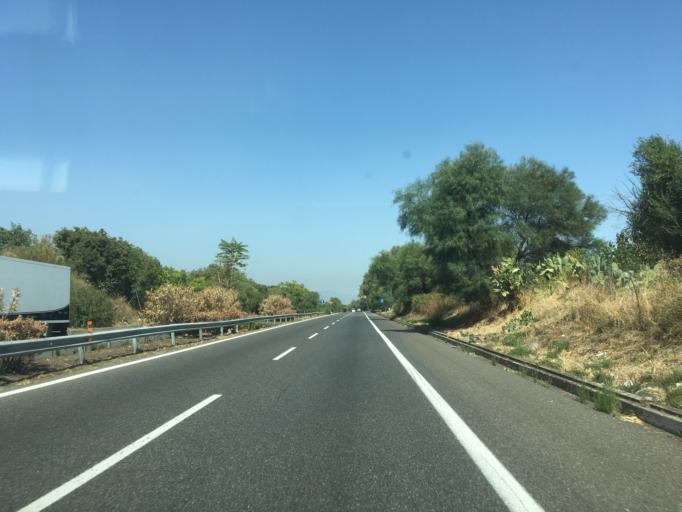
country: IT
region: Sicily
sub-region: Catania
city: Linera
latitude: 37.6493
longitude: 15.1484
